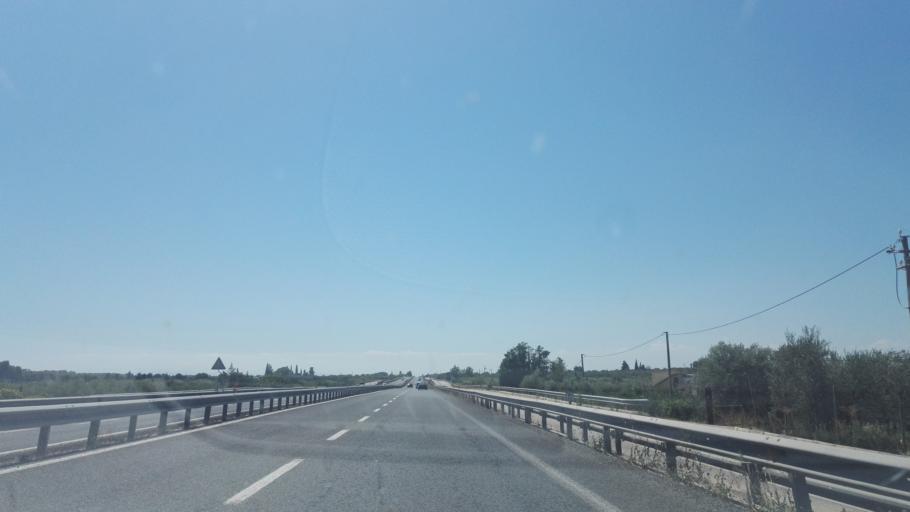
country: IT
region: Apulia
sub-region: Provincia di Taranto
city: Palagiano
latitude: 40.5216
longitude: 17.0241
